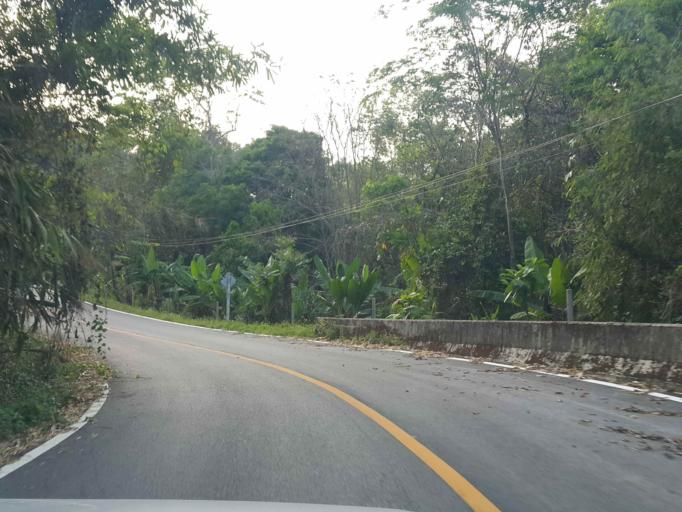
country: TH
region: Chiang Mai
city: Mae On
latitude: 18.9605
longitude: 99.3313
